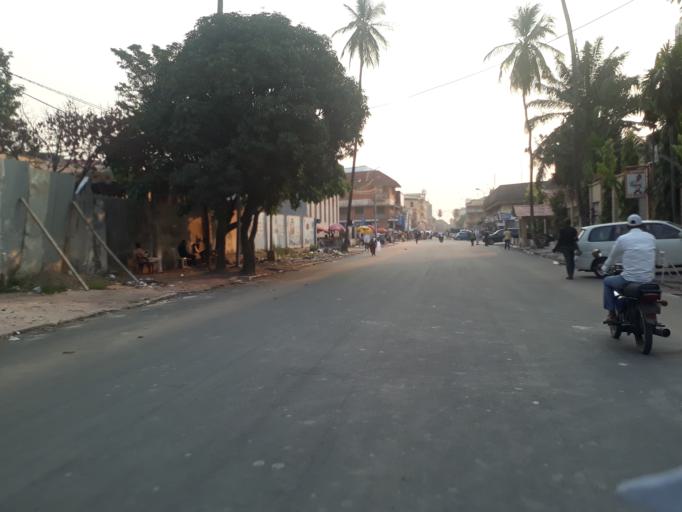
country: CD
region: Kinshasa
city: Kinshasa
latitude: -4.3042
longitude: 15.3147
